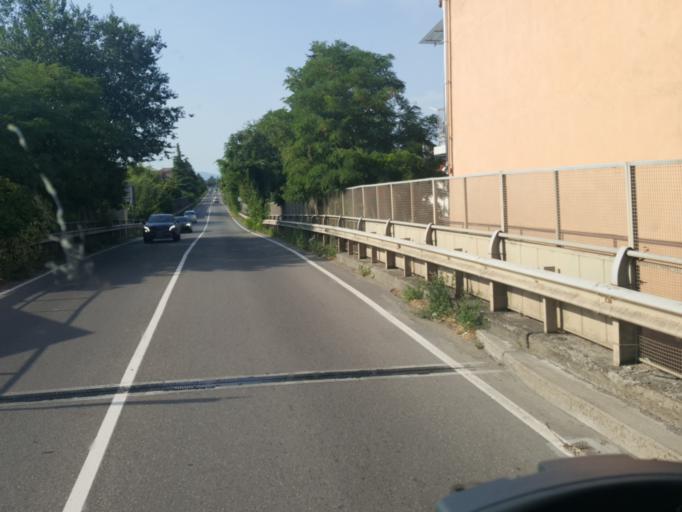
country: IT
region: Piedmont
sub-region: Provincia di Alessandria
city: Tortona
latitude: 44.8950
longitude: 8.8557
